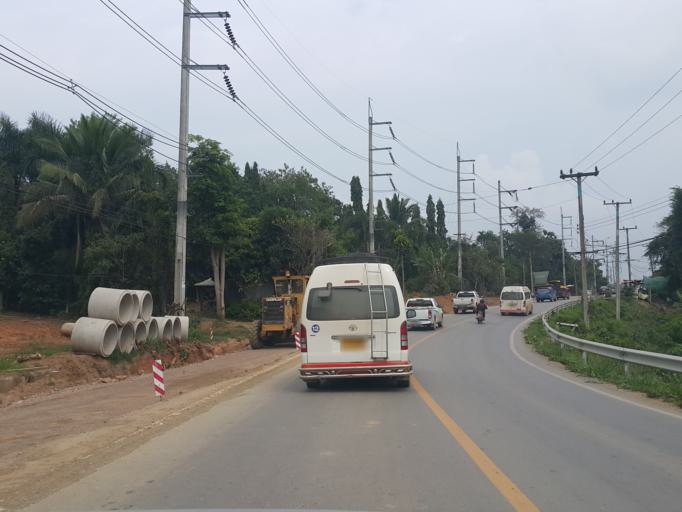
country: TH
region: Chiang Mai
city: Mae Taeng
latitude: 19.0947
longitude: 98.8726
